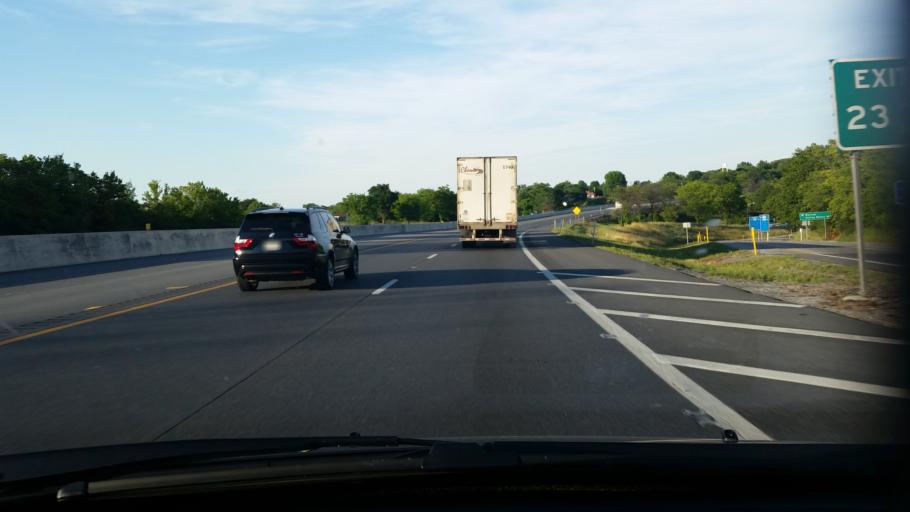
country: US
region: Maryland
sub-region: Washington County
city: Williamsport
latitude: 39.5780
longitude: -77.8803
